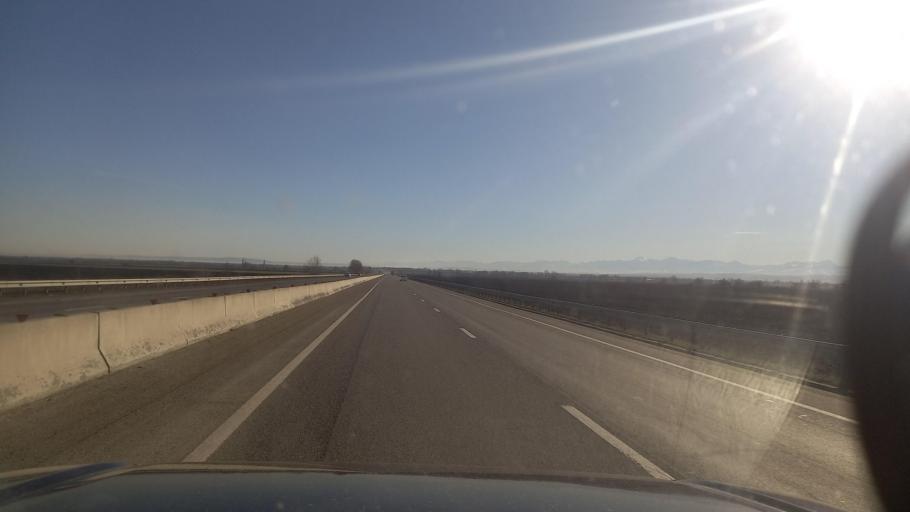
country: RU
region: Kabardino-Balkariya
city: Nartan
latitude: 43.5853
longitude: 43.6861
